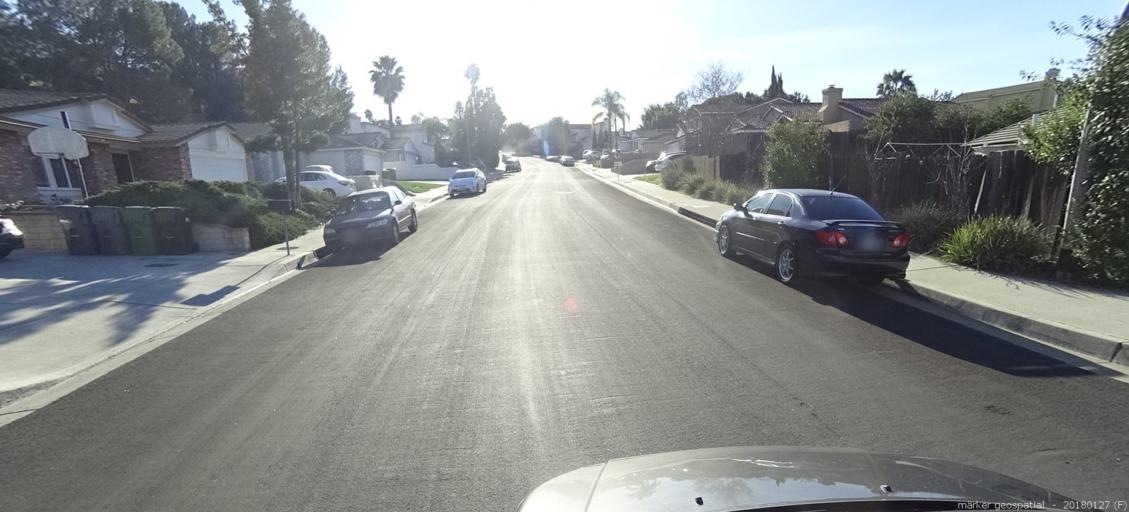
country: US
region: California
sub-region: Los Angeles County
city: Diamond Bar
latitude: 34.0245
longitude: -117.7920
